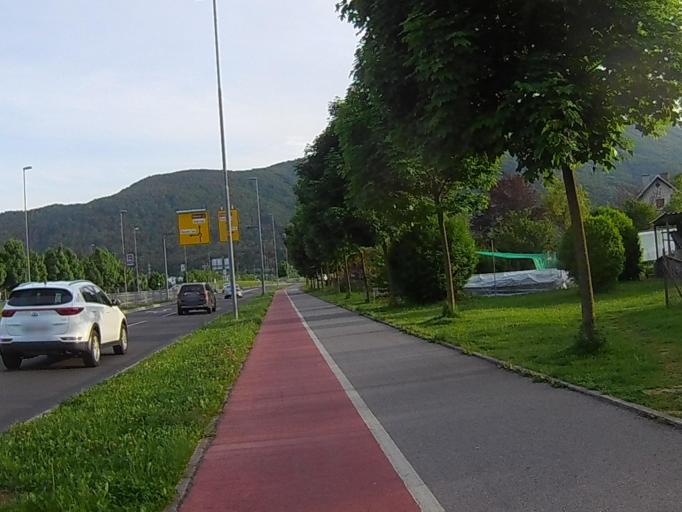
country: SI
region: Maribor
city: Pekre
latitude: 46.5441
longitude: 15.6187
